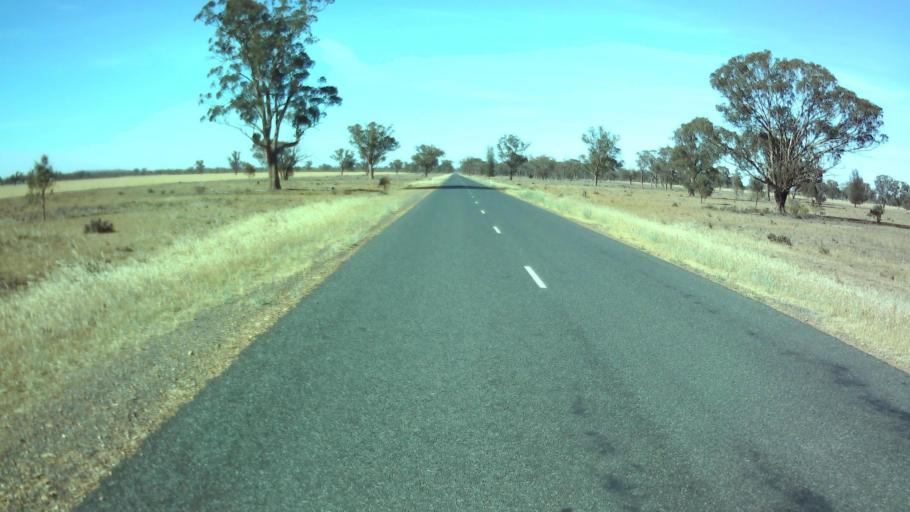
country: AU
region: New South Wales
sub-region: Weddin
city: Grenfell
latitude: -34.0814
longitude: 147.8957
